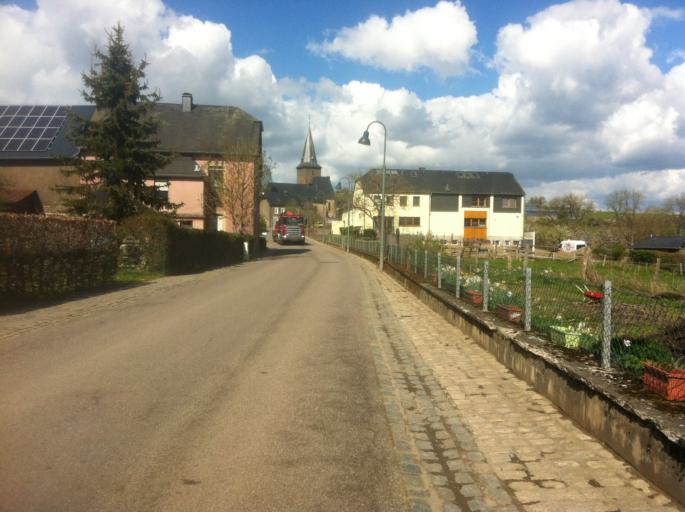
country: LU
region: Diekirch
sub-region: Canton de Clervaux
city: Clervaux
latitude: 50.0309
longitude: 6.0361
